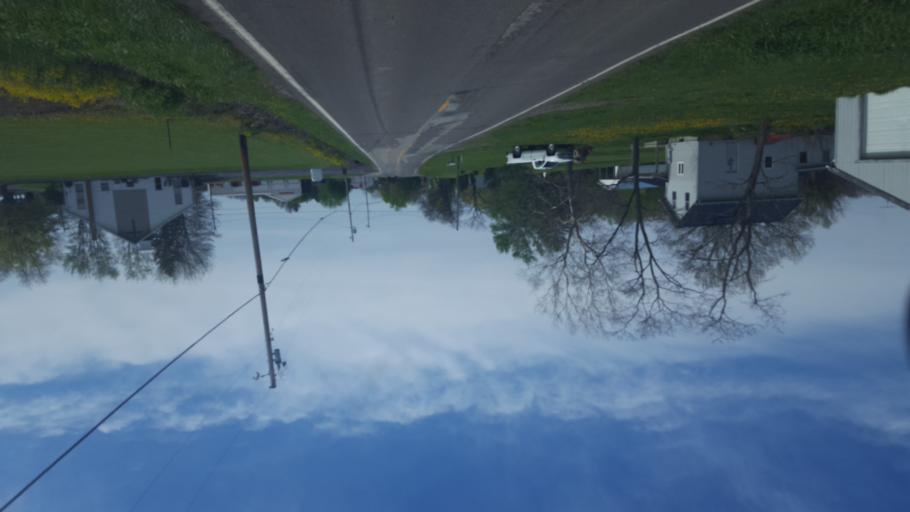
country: US
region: Ohio
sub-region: Richland County
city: Shelby
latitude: 40.8590
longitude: -82.6106
